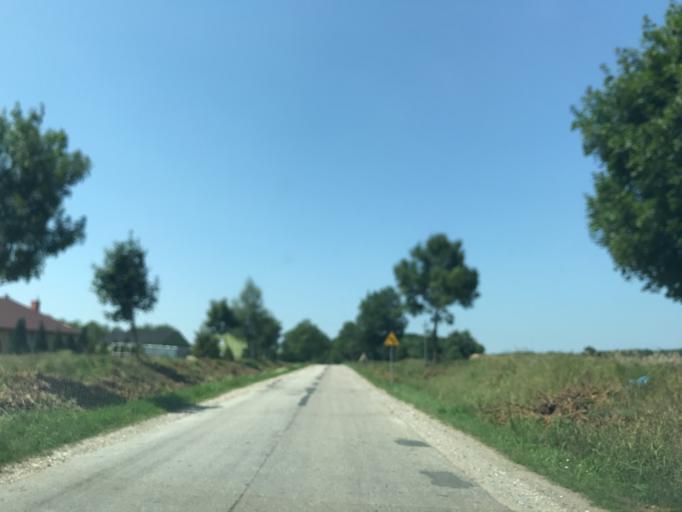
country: PL
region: Kujawsko-Pomorskie
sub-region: Powiat lipnowski
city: Chrostkowo
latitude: 52.9893
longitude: 19.2915
